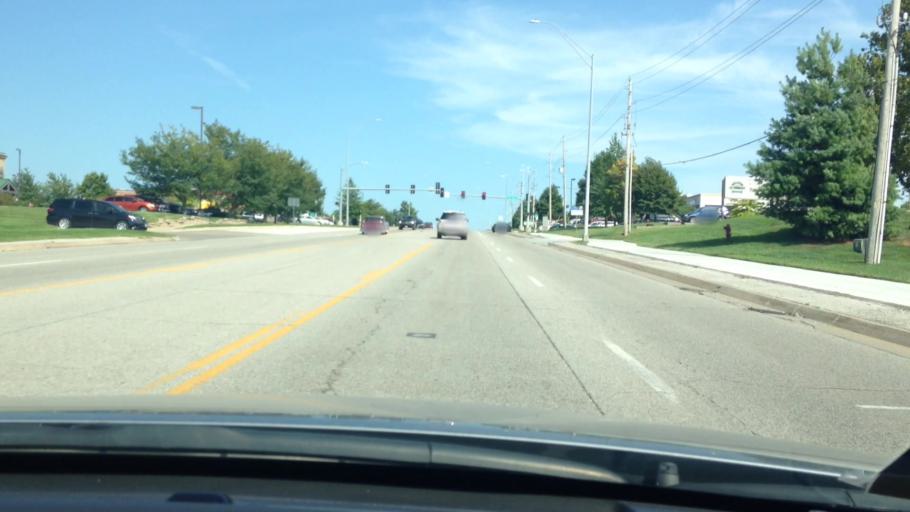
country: US
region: Missouri
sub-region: Cass County
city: Belton
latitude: 38.8139
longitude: -94.5189
